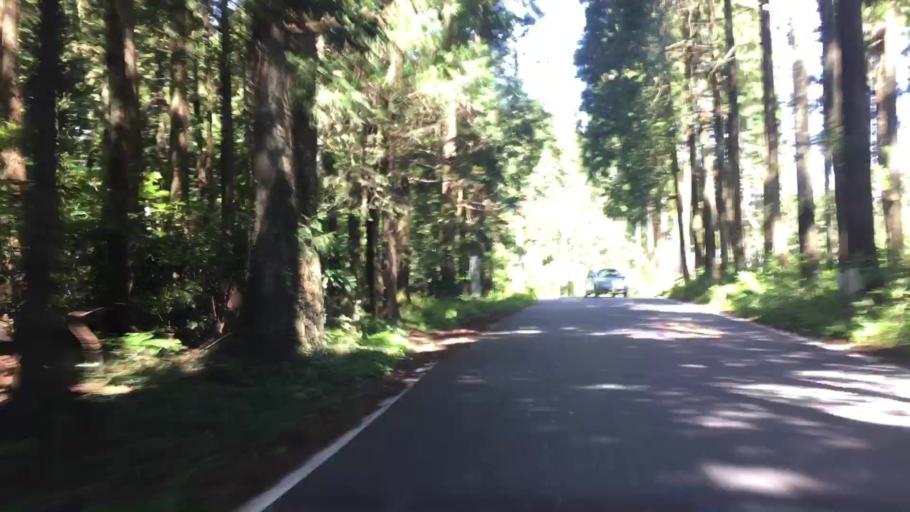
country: JP
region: Tochigi
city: Imaichi
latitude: 36.7105
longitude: 139.7516
